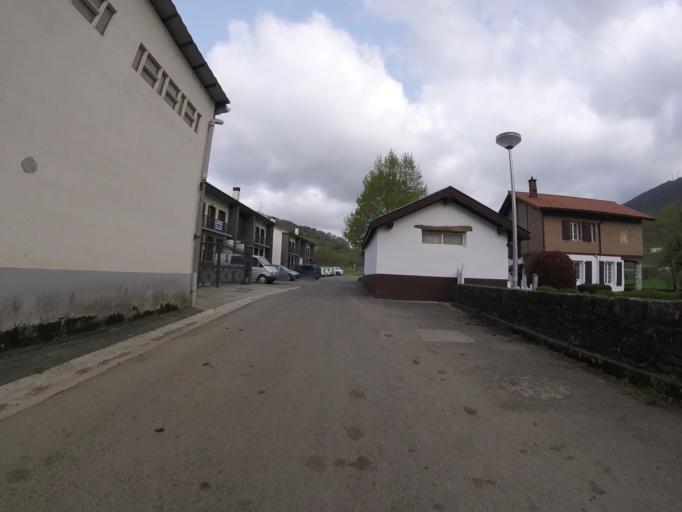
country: ES
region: Basque Country
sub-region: Provincia de Guipuzcoa
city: Berastegui
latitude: 43.1243
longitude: -1.9847
